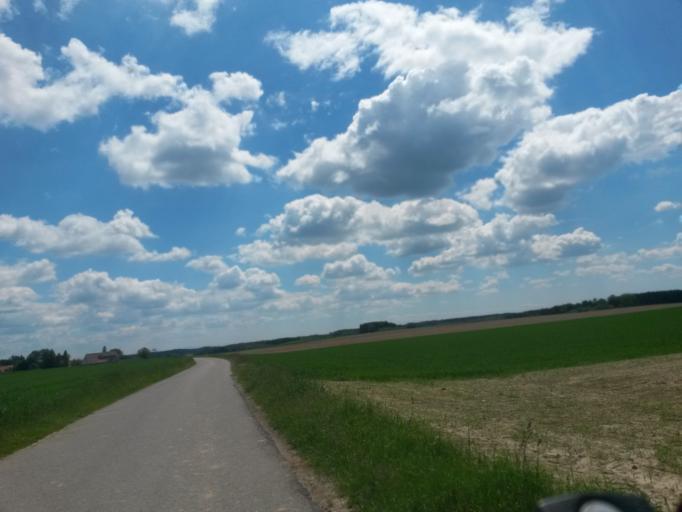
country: DE
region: Baden-Wuerttemberg
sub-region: Tuebingen Region
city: Ingoldingen
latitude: 47.9909
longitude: 9.7113
